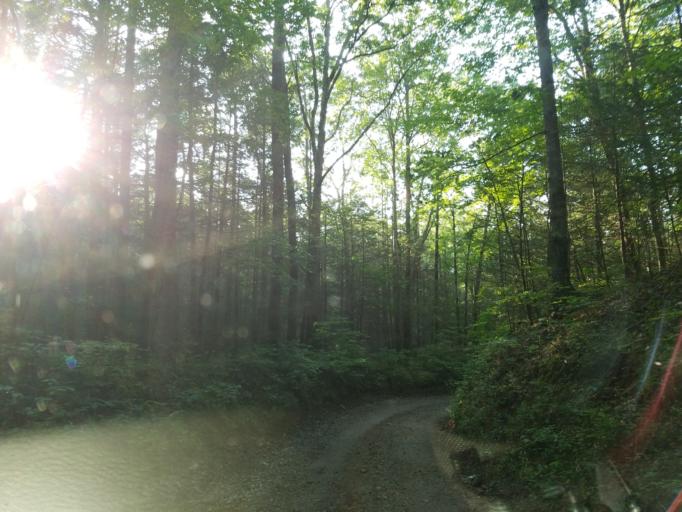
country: US
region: Georgia
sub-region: Lumpkin County
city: Dahlonega
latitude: 34.6564
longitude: -84.0855
